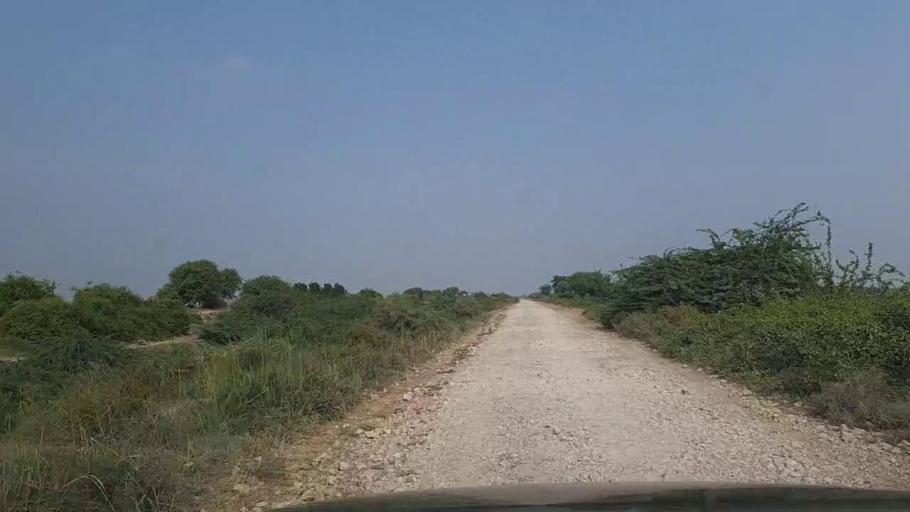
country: PK
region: Sindh
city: Thatta
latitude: 24.7455
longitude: 67.8070
